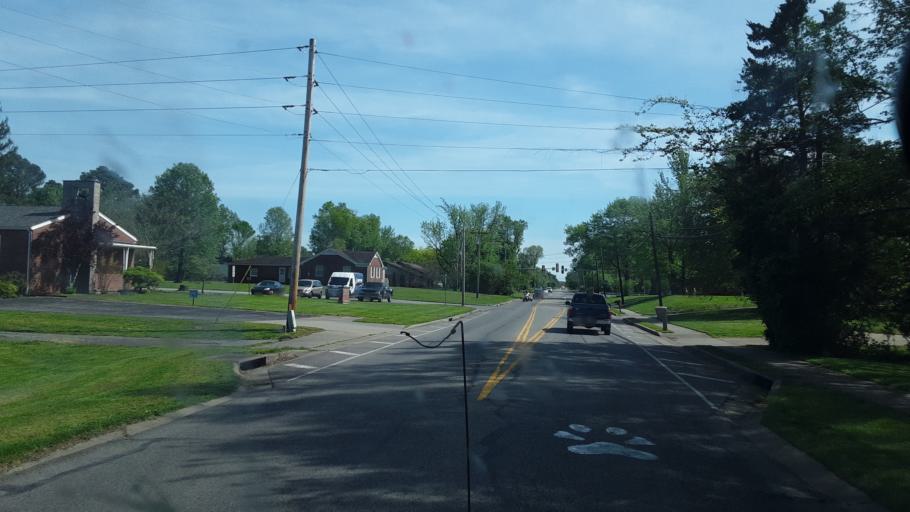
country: US
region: Illinois
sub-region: Jackson County
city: Carbondale
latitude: 37.7197
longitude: -89.1853
